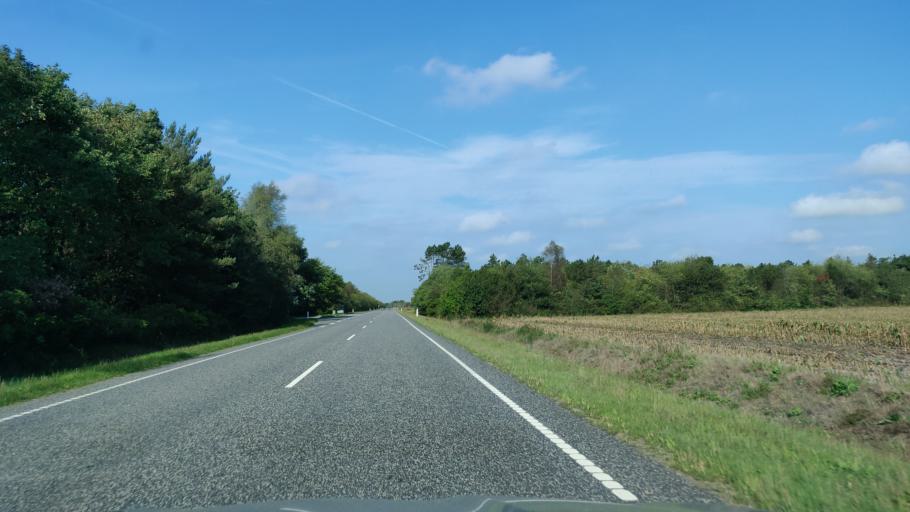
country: DK
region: Central Jutland
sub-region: Herning Kommune
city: Sunds
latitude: 56.2453
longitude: 9.0760
